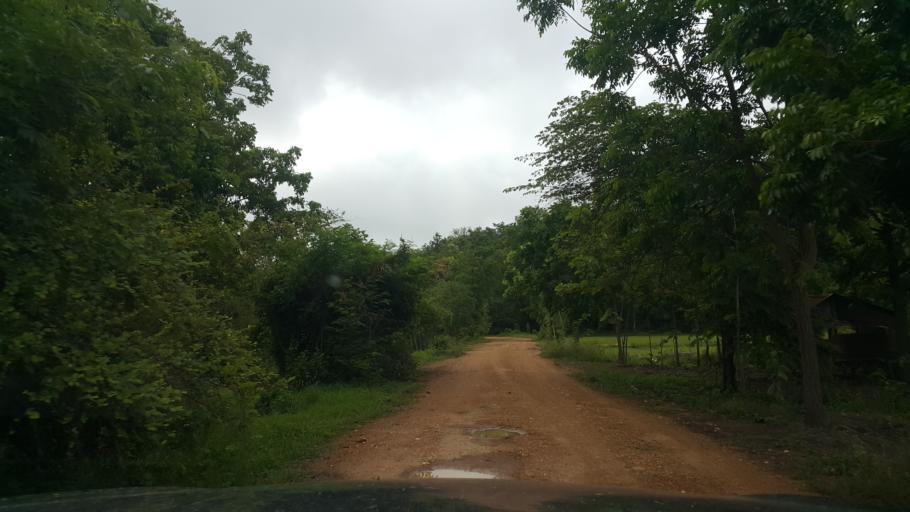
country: TH
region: Sukhothai
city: Sawankhalok
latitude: 17.3059
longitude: 99.7120
